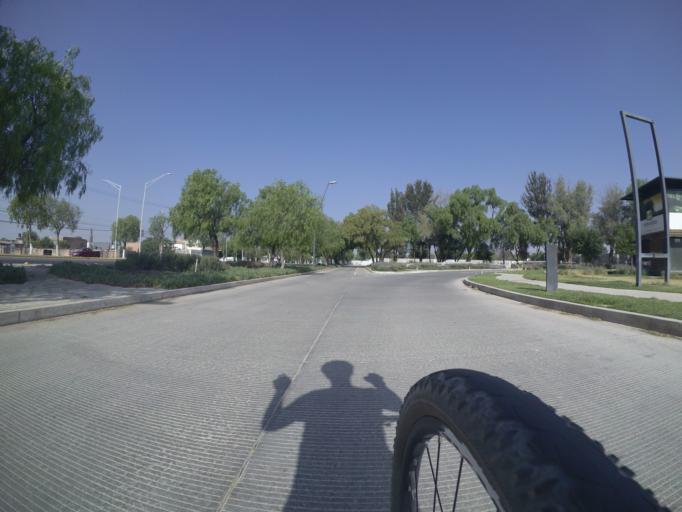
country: MX
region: Aguascalientes
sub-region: Jesus Maria
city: El Llano
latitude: 21.9496
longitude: -102.3166
